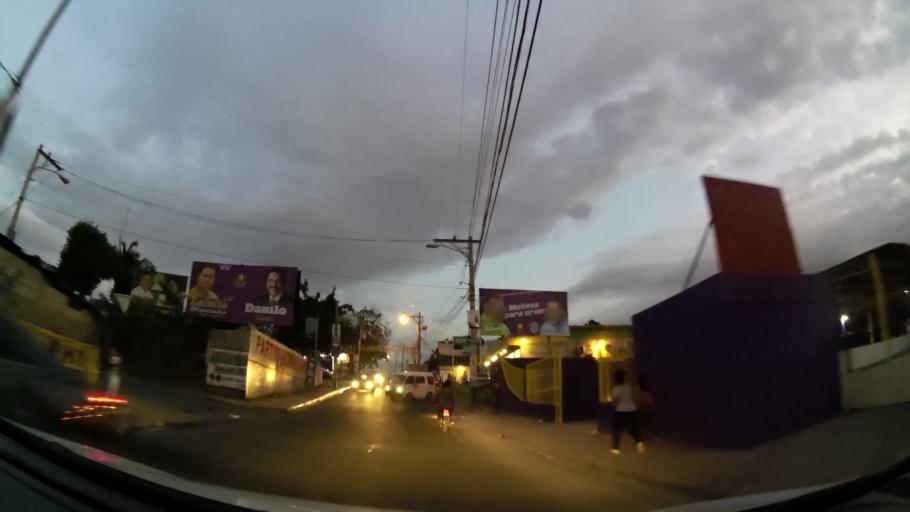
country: DO
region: Santo Domingo
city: Santo Domingo Oeste
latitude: 18.5221
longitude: -70.0179
